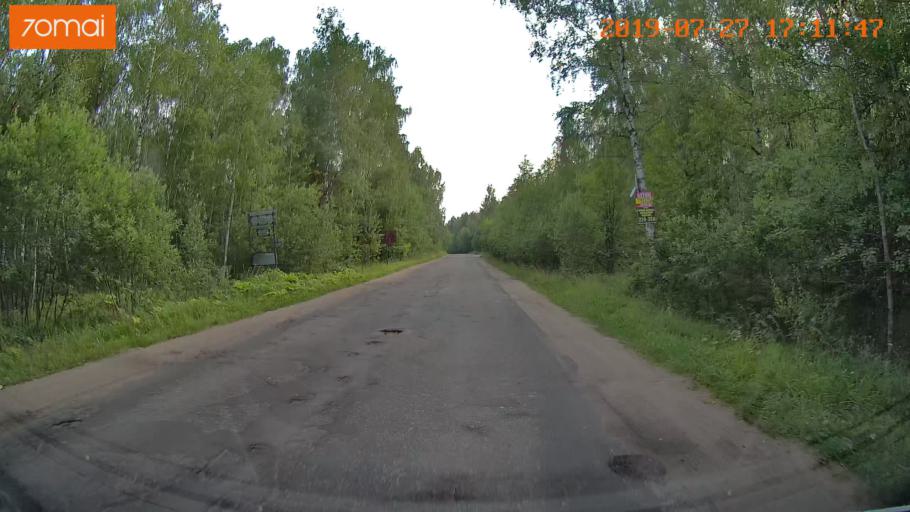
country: RU
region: Ivanovo
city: Novo-Talitsy
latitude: 57.0627
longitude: 40.8645
